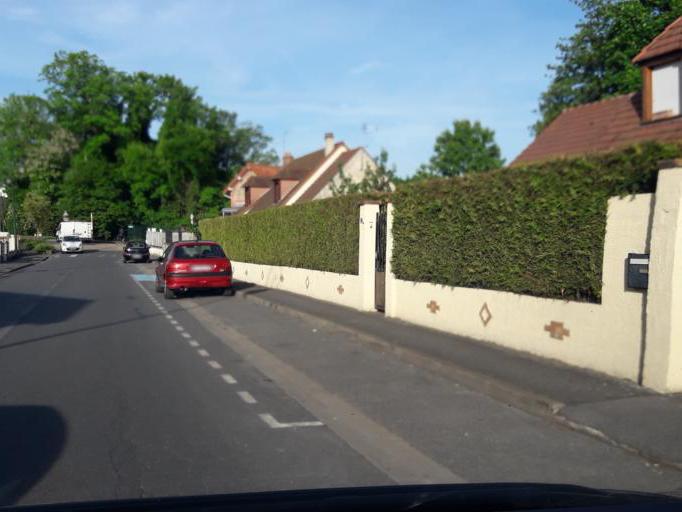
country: FR
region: Ile-de-France
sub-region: Departement de l'Essonne
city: Ballancourt-sur-Essonne
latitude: 48.5317
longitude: 2.3693
